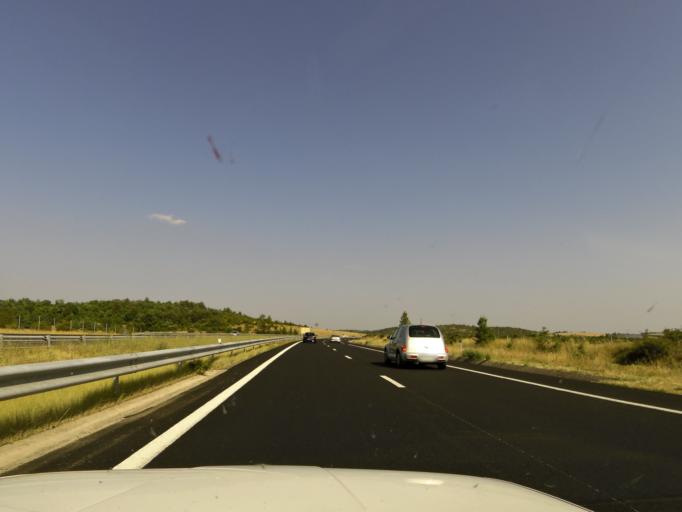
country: FR
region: Midi-Pyrenees
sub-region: Departement de l'Aveyron
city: La Cavalerie
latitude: 43.9210
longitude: 3.2456
